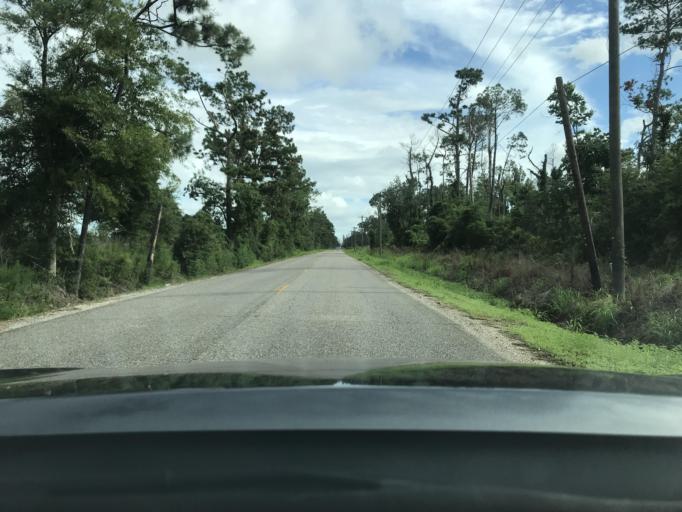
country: US
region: Louisiana
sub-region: Calcasieu Parish
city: Westlake
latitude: 30.2731
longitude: -93.2751
